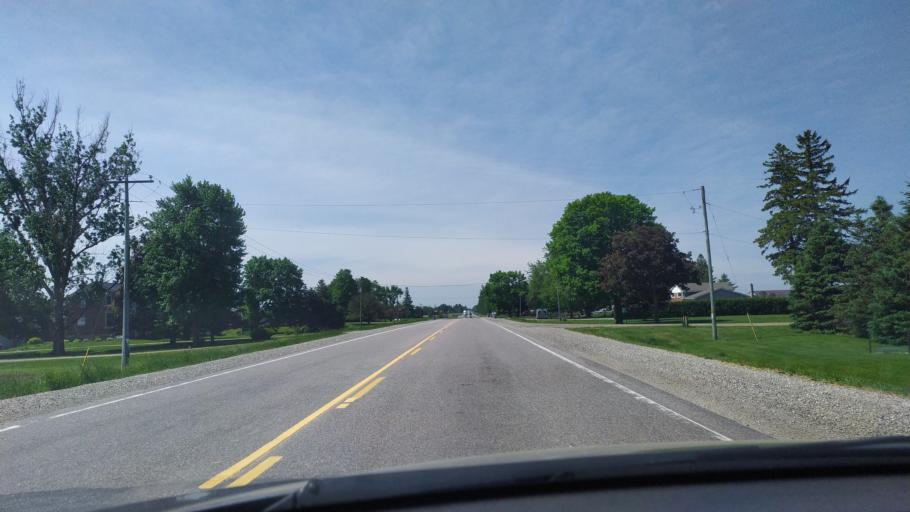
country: CA
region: Ontario
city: Stratford
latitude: 43.3221
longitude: -81.0243
